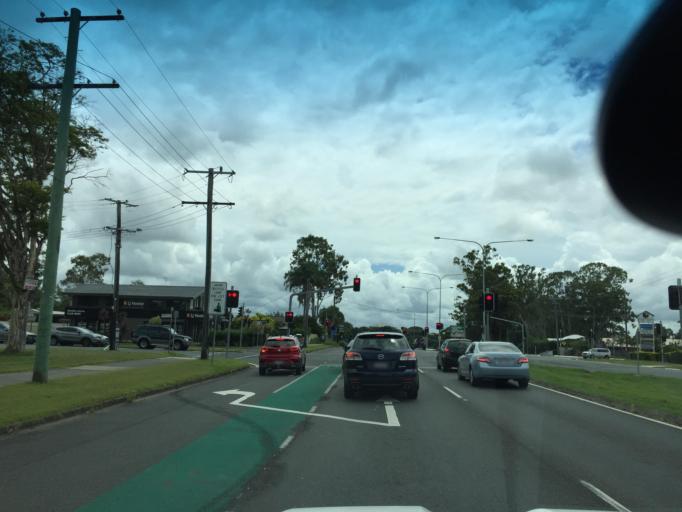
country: AU
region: Queensland
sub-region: Moreton Bay
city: Caboolture South
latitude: -27.0928
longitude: 152.9498
